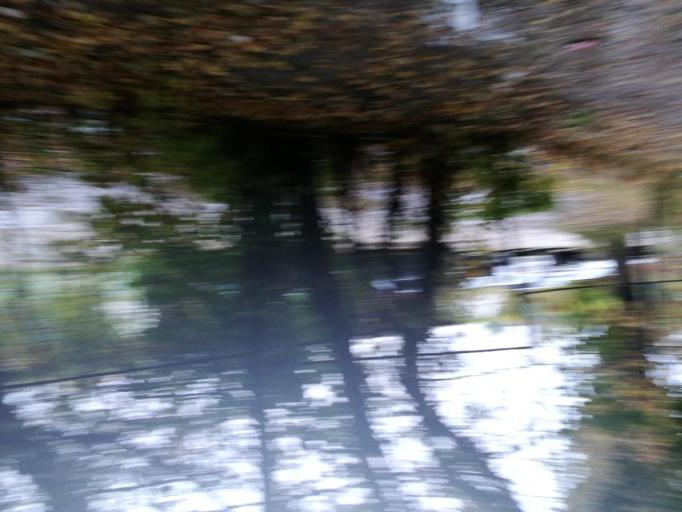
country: RO
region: Ilfov
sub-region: Comuna Chiajna
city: Rosu
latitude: 44.4484
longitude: 26.0513
